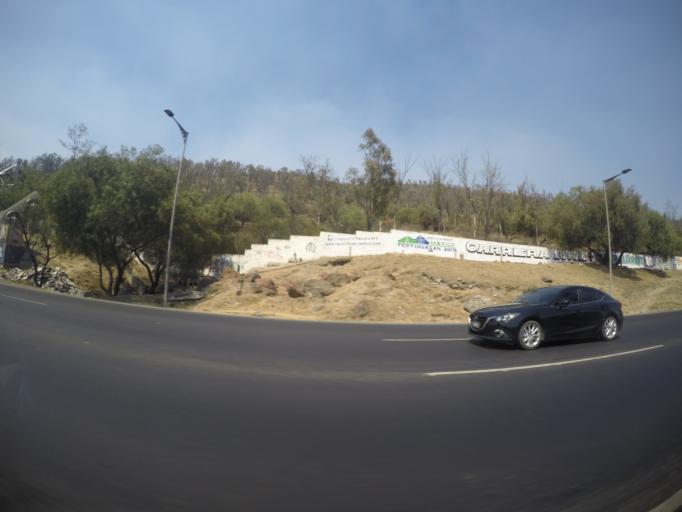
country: MX
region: Mexico City
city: Gustavo A. Madero
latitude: 19.5048
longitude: -99.1120
